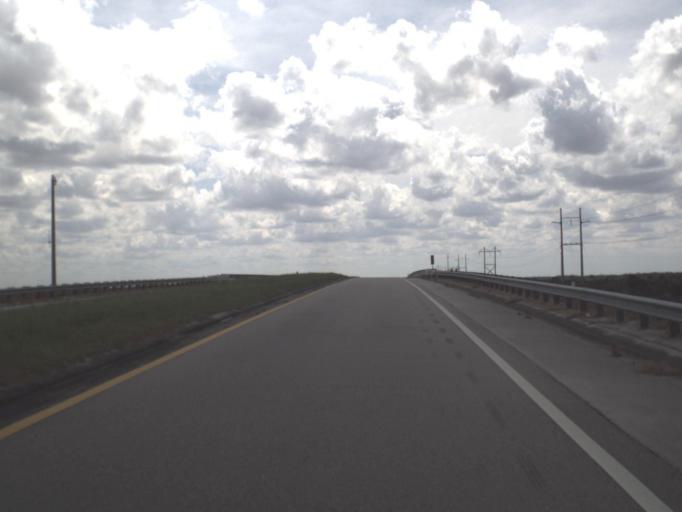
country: US
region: Florida
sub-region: Collier County
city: Immokalee
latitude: 26.1560
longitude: -81.3451
